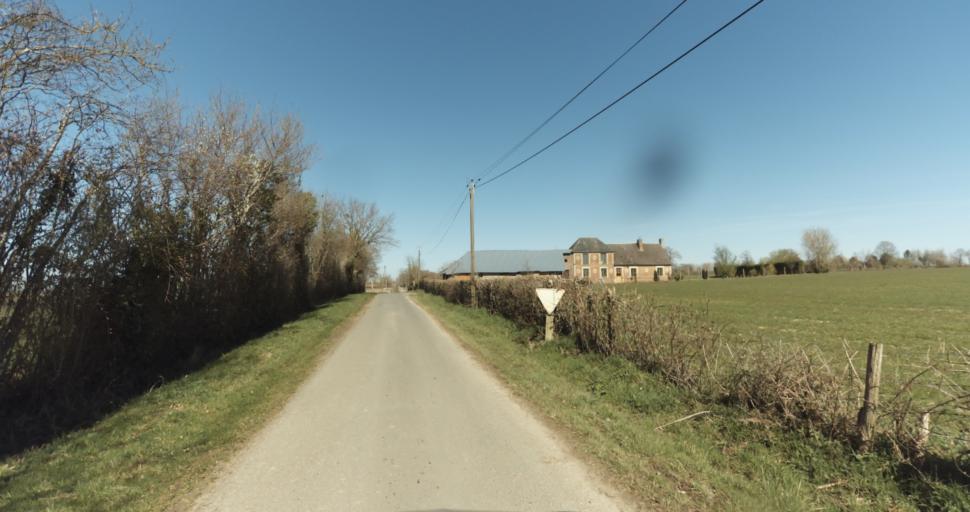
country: FR
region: Lower Normandy
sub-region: Departement du Calvados
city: Livarot
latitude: 49.0125
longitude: 0.1048
